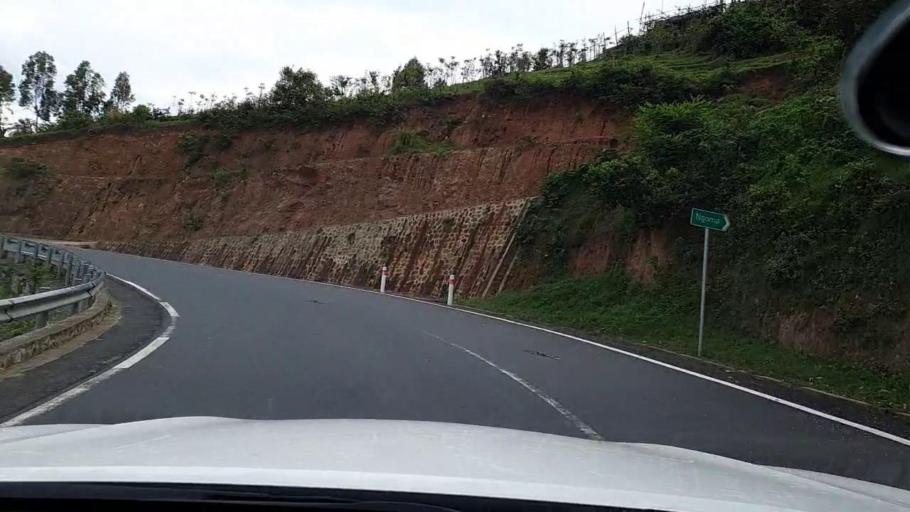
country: RW
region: Western Province
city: Kibuye
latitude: -2.1766
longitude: 29.2898
